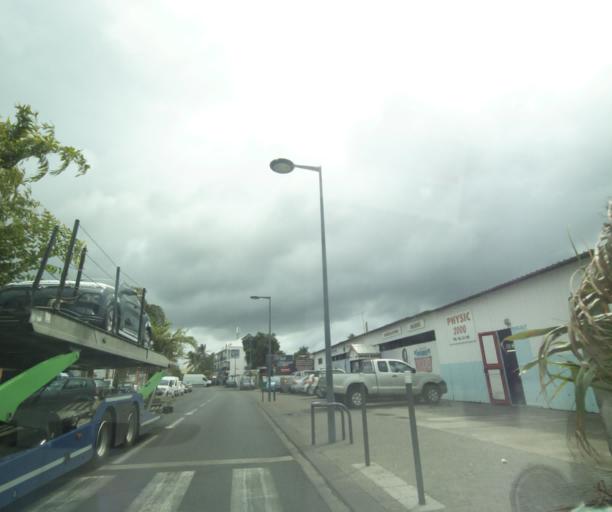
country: RE
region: Reunion
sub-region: Reunion
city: Saint-Paul
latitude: -20.9982
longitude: 55.2830
